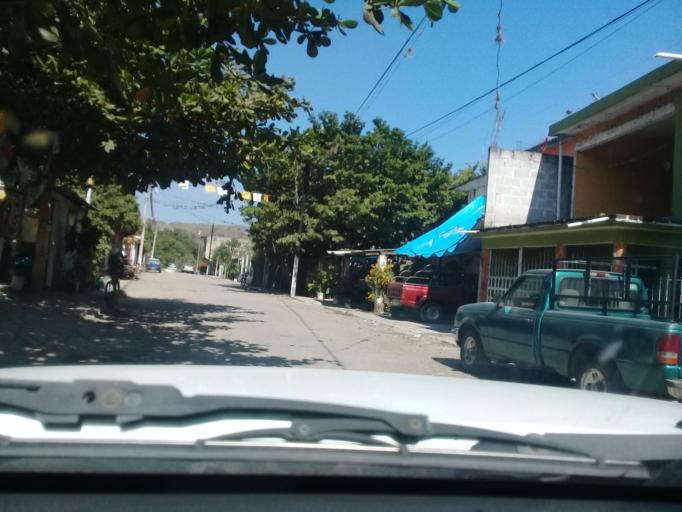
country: MX
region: Veracruz
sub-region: Emiliano Zapata
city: Plan del Rio
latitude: 19.4261
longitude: -96.6132
